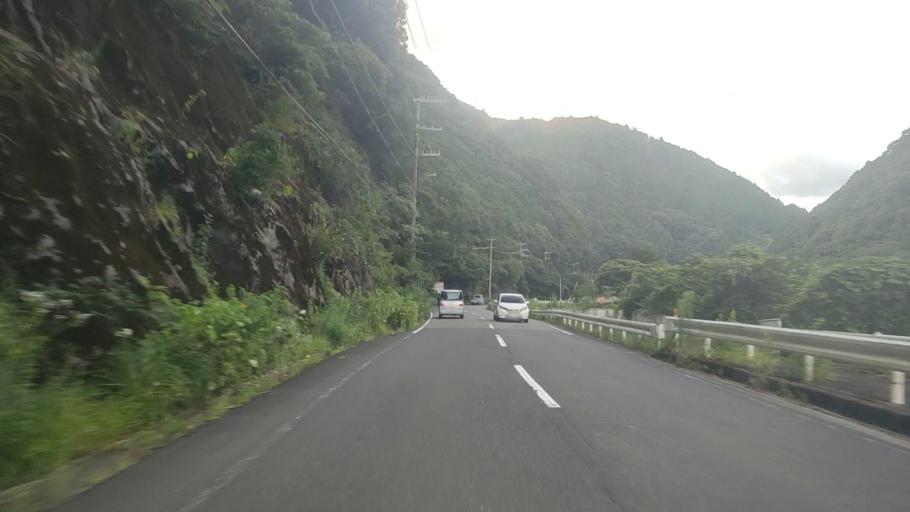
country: JP
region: Wakayama
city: Tanabe
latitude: 33.7695
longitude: 135.5000
